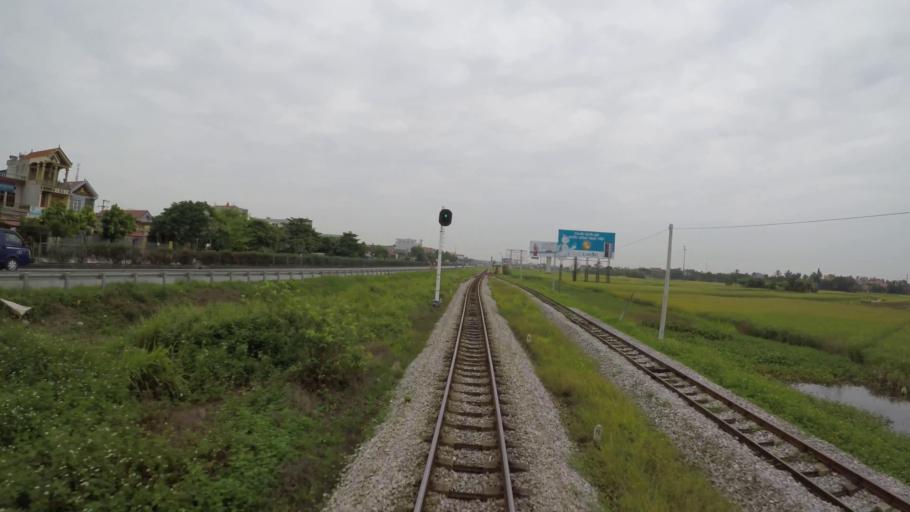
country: VN
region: Hai Duong
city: Phu Thai
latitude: 20.9312
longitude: 106.5533
